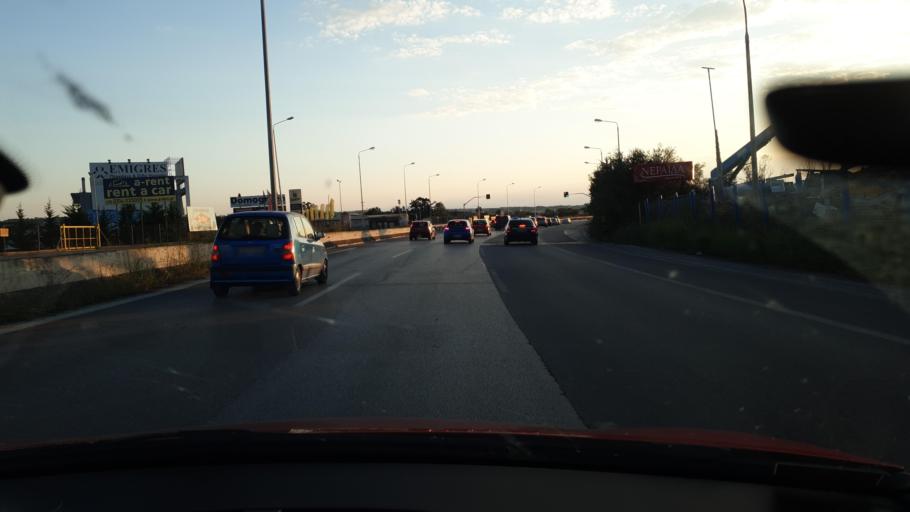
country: GR
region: Central Macedonia
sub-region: Nomos Thessalonikis
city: Neo Rysi
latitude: 40.5139
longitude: 22.9892
